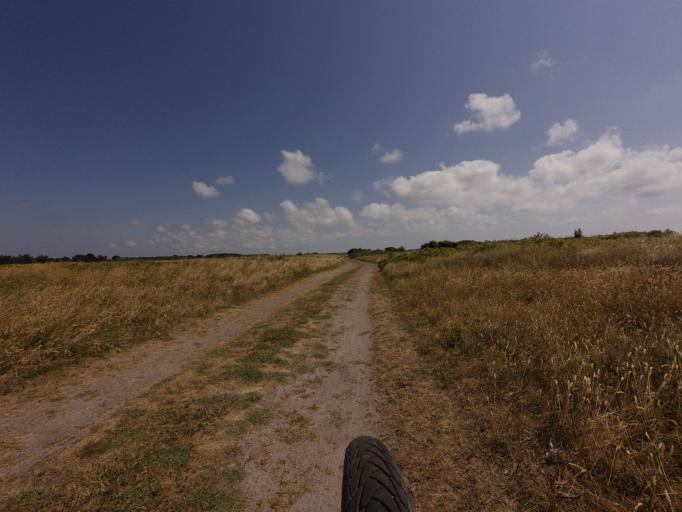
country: DK
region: North Denmark
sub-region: Laeso Kommune
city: Byrum
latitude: 57.2510
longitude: 10.8831
